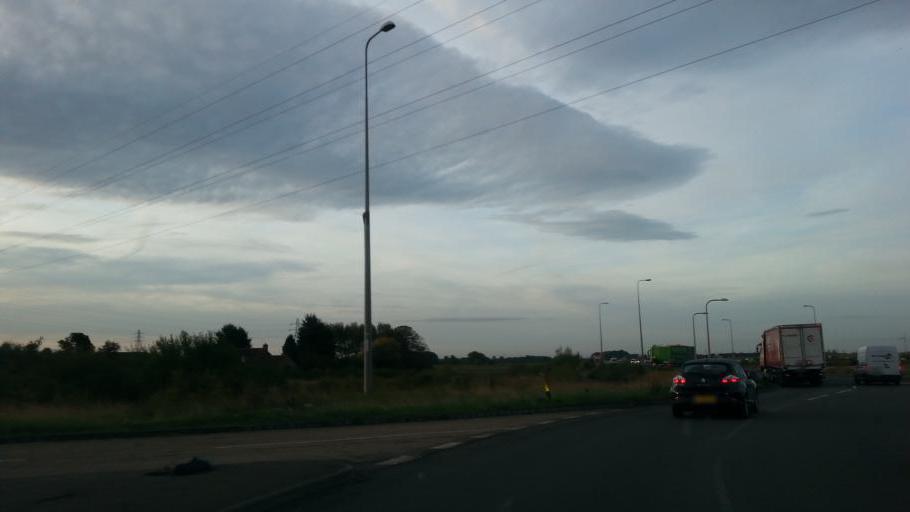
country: GB
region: England
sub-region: Nottinghamshire
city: Newark on Trent
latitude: 53.0640
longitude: -0.8349
